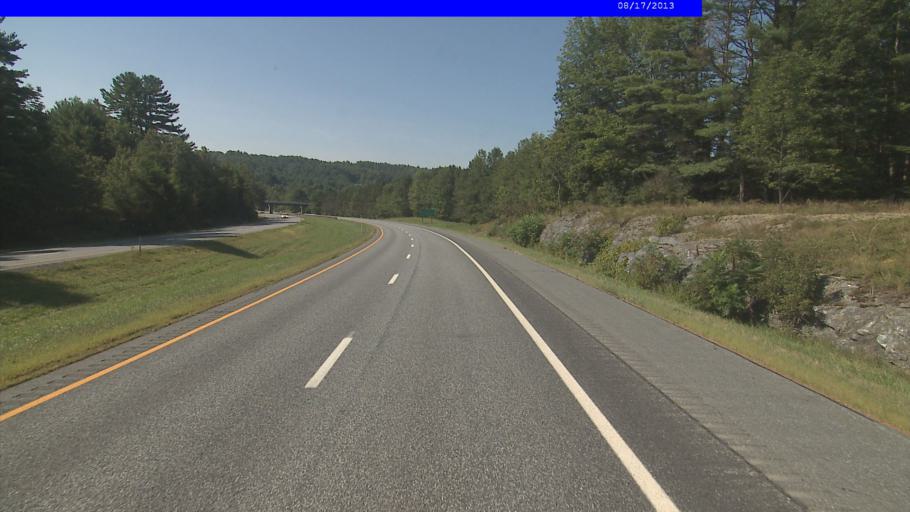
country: US
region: Vermont
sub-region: Windsor County
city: Windsor
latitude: 43.4175
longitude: -72.4142
